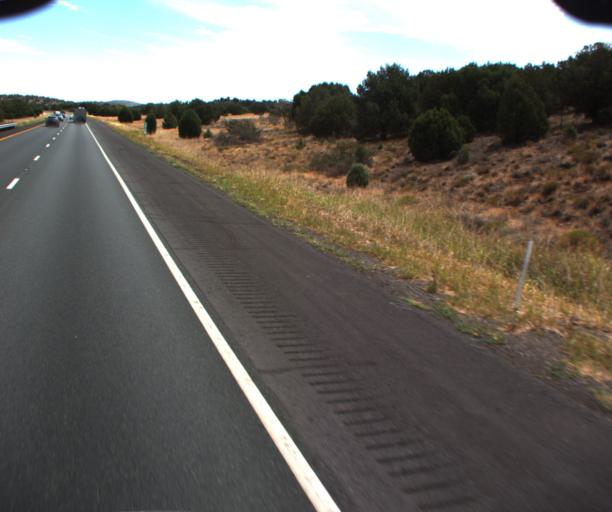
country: US
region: Arizona
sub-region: Yavapai County
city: Camp Verde
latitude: 34.4844
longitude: -112.0140
